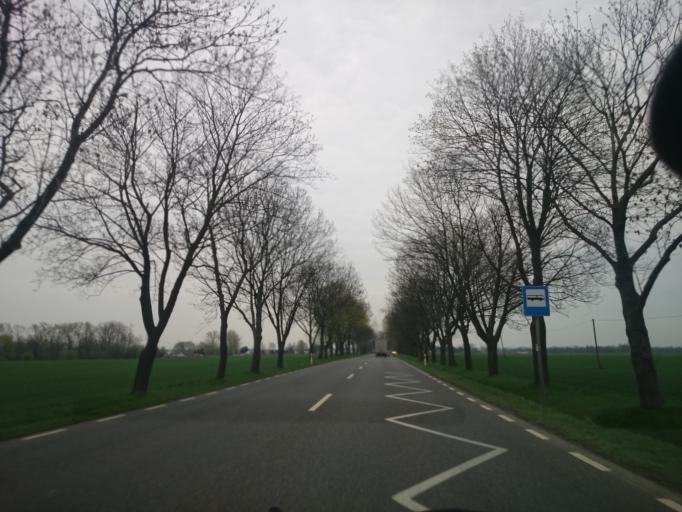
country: PL
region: Opole Voivodeship
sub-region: Powiat nyski
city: Otmuchow
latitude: 50.4485
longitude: 17.0940
